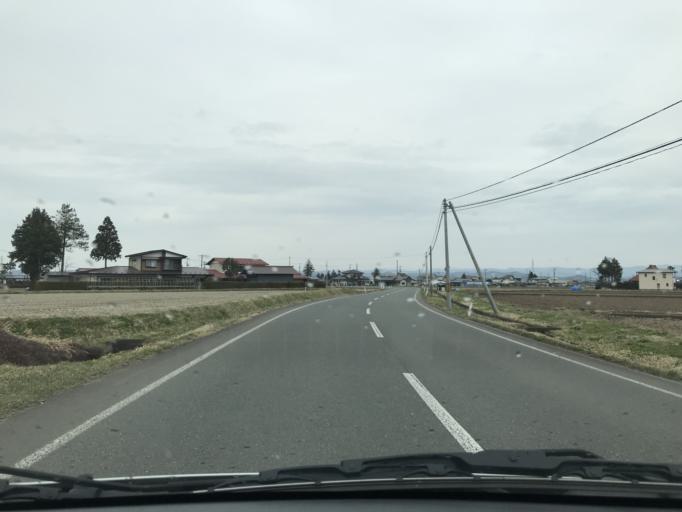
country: JP
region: Iwate
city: Mizusawa
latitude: 39.1716
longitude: 141.1119
